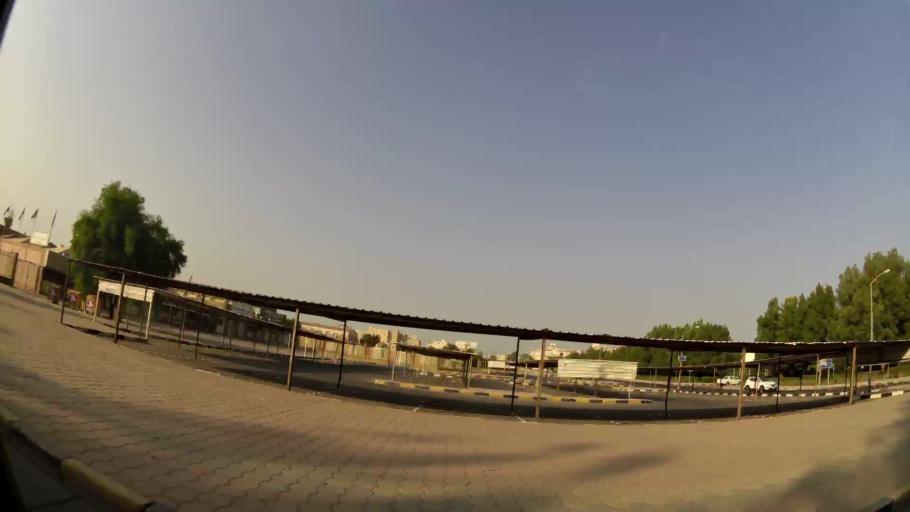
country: KW
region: Muhafazat Hawalli
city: Ar Rumaythiyah
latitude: 29.3157
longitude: 48.0812
